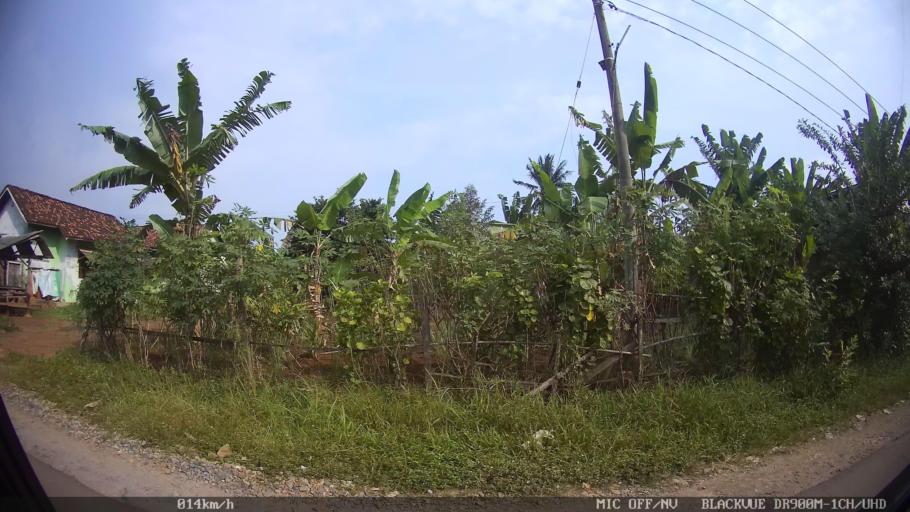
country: ID
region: Lampung
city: Kedaton
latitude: -5.3557
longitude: 105.2215
